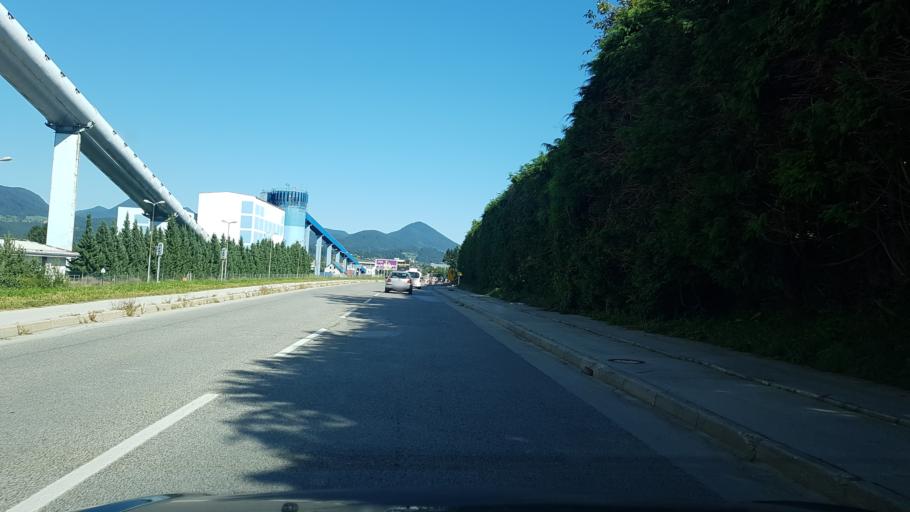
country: SI
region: Sostanj
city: Sostanj
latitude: 46.3685
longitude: 15.0764
